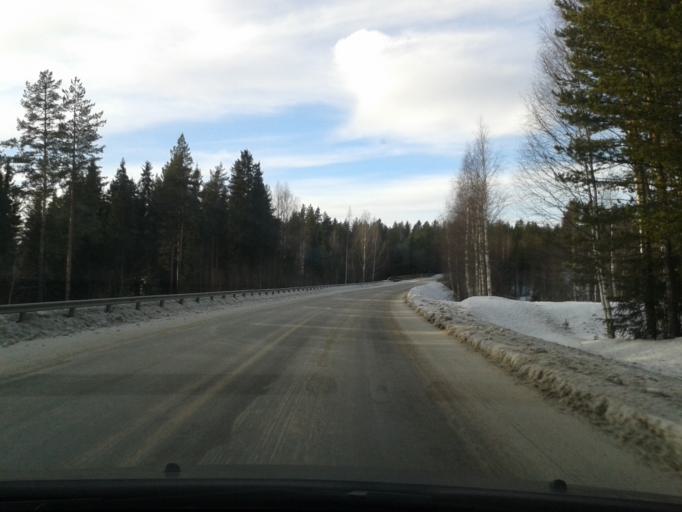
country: SE
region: Vaesternorrland
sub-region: OErnskoeldsviks Kommun
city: Bredbyn
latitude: 63.5303
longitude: 17.9747
